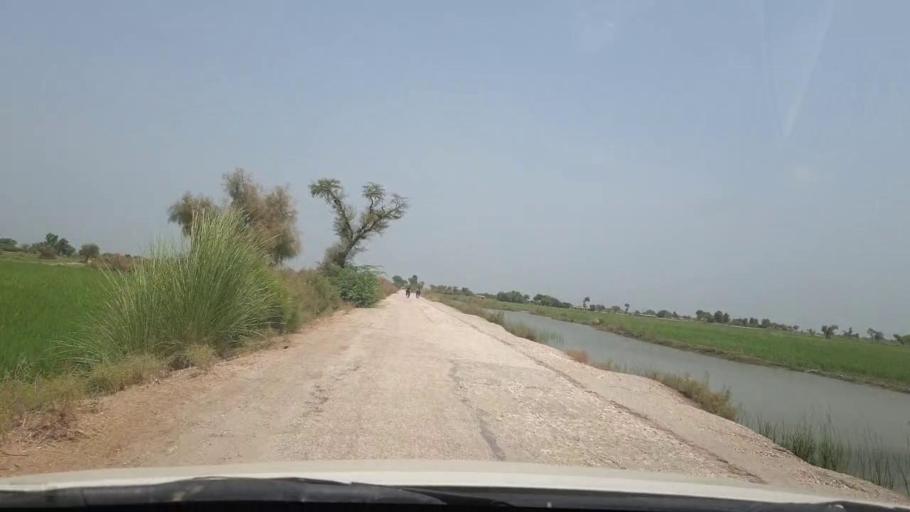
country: PK
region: Sindh
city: Rustam jo Goth
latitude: 28.0386
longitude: 68.8143
